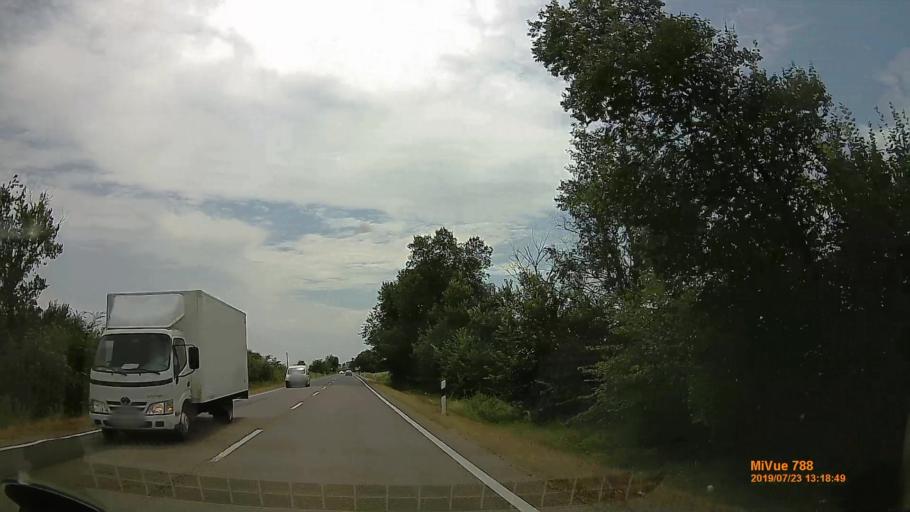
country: HU
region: Hajdu-Bihar
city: Polgar
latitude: 47.8805
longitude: 21.1463
